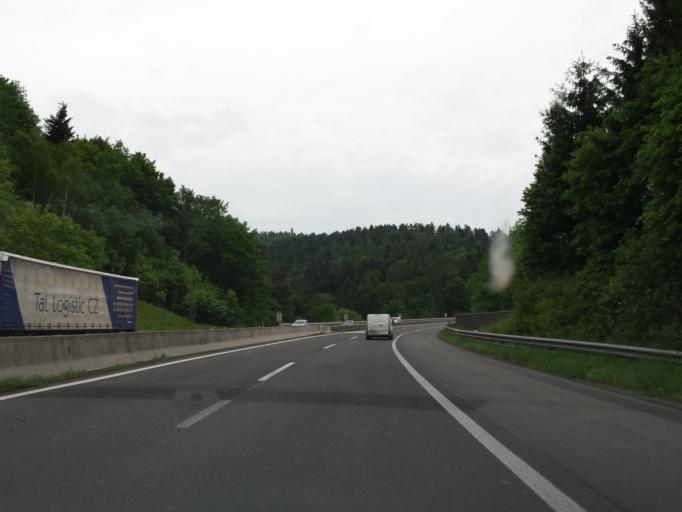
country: AT
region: Lower Austria
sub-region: Politischer Bezirk Neunkirchen
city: Edlitz
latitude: 47.5949
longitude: 16.1237
